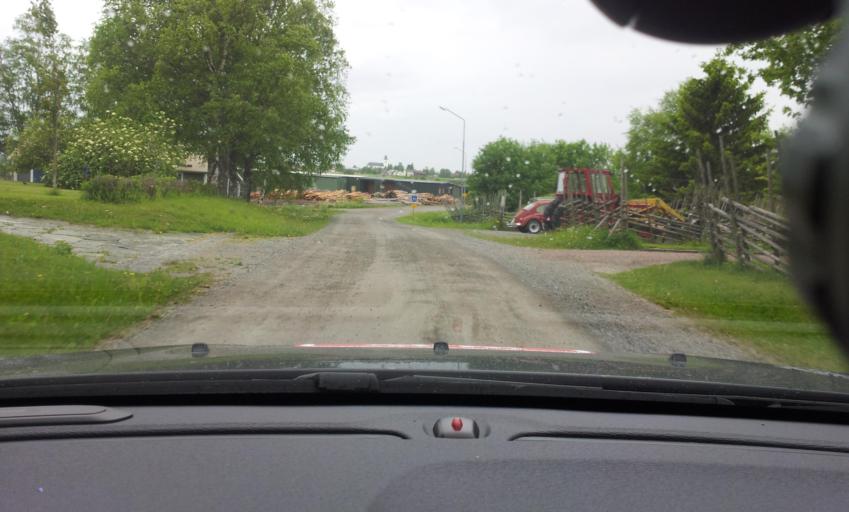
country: SE
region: Jaemtland
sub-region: OEstersunds Kommun
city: Ostersund
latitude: 62.9839
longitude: 14.5873
